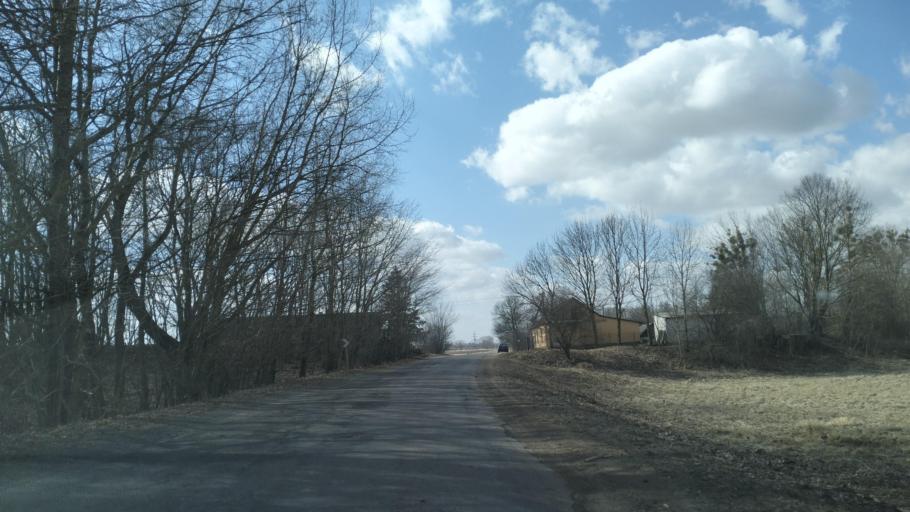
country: BY
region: Grodnenskaya
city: Karelichy
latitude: 53.6603
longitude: 26.1261
